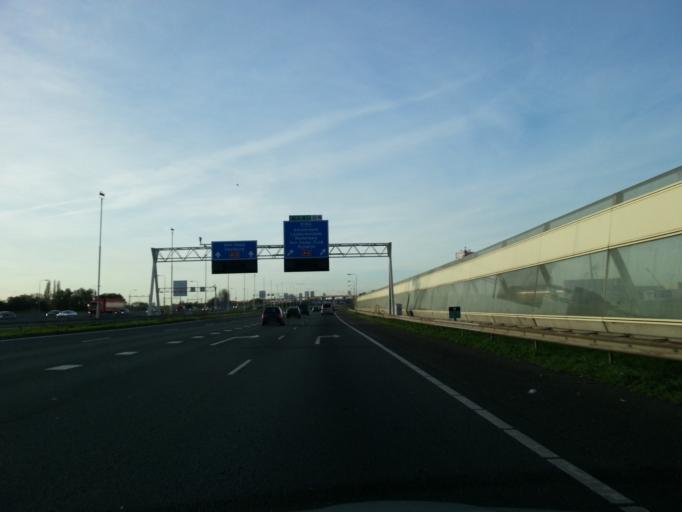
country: NL
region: South Holland
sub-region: Gemeente Den Haag
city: Ypenburg
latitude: 52.0571
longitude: 4.3895
